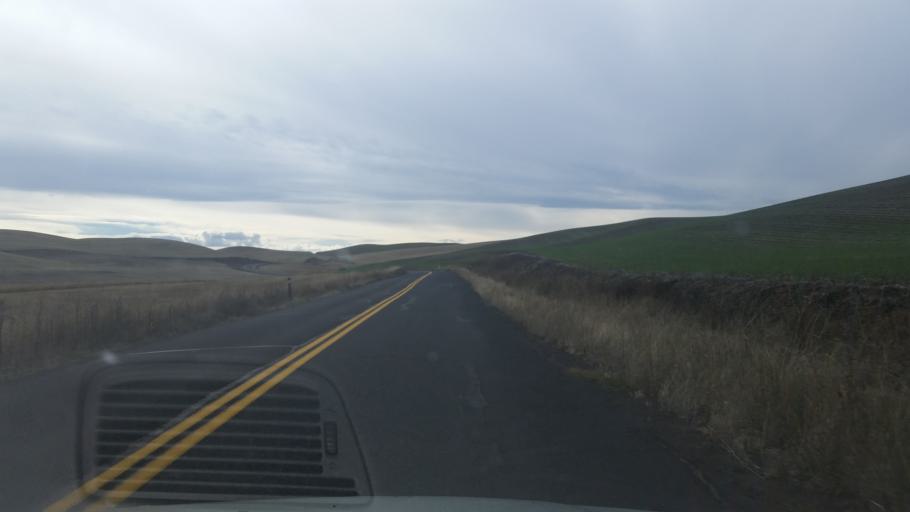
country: US
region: Washington
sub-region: Spokane County
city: Cheney
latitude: 47.2851
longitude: -117.4877
